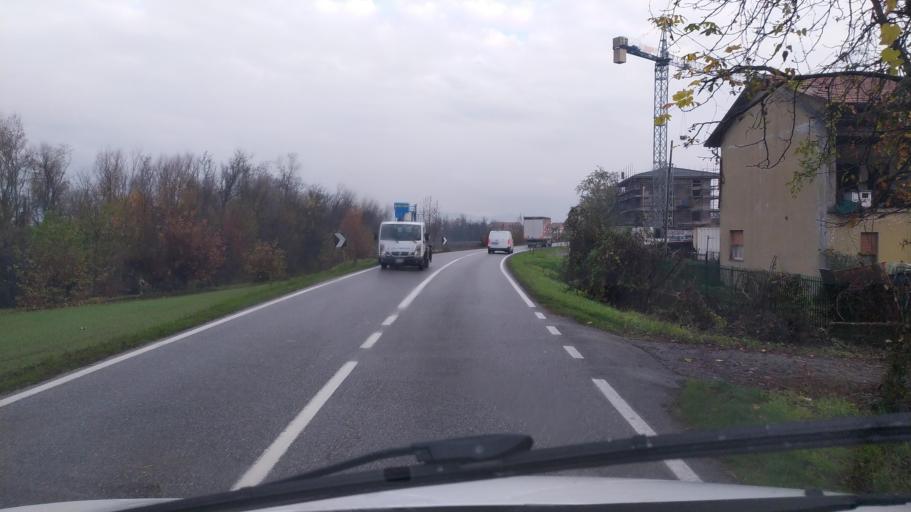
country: IT
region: Lombardy
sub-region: Provincia di Brescia
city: Pontoglio
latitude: 45.5566
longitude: 9.8588
